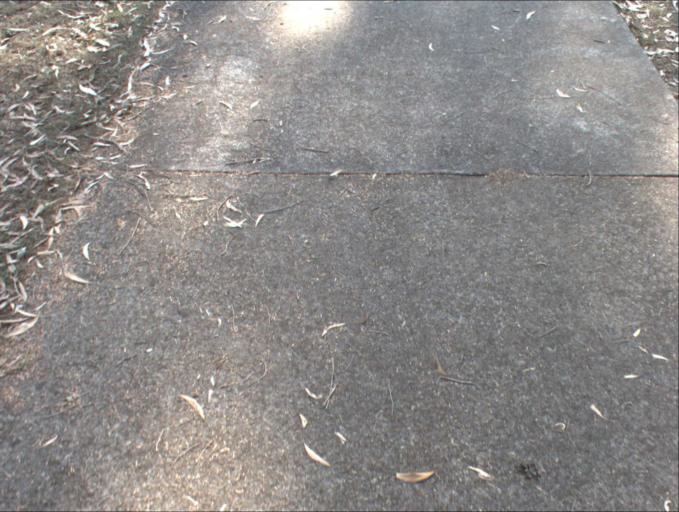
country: AU
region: Queensland
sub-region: Logan
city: Beenleigh
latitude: -27.7010
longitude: 153.1926
